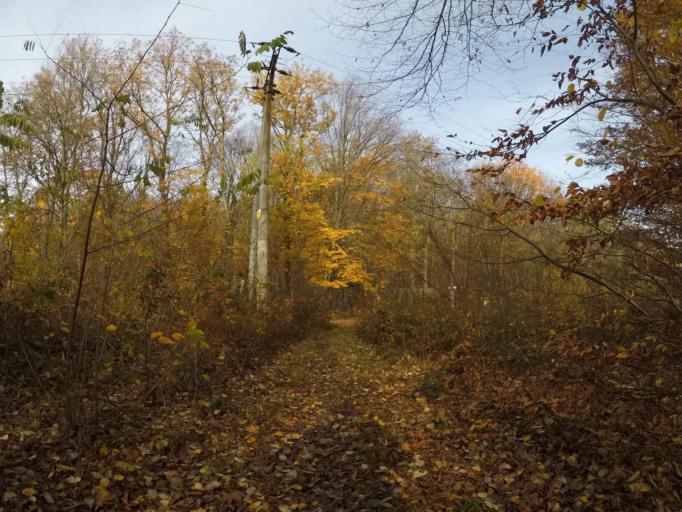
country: SK
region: Presovsky
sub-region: Okres Presov
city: Presov
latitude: 48.9264
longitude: 21.2190
